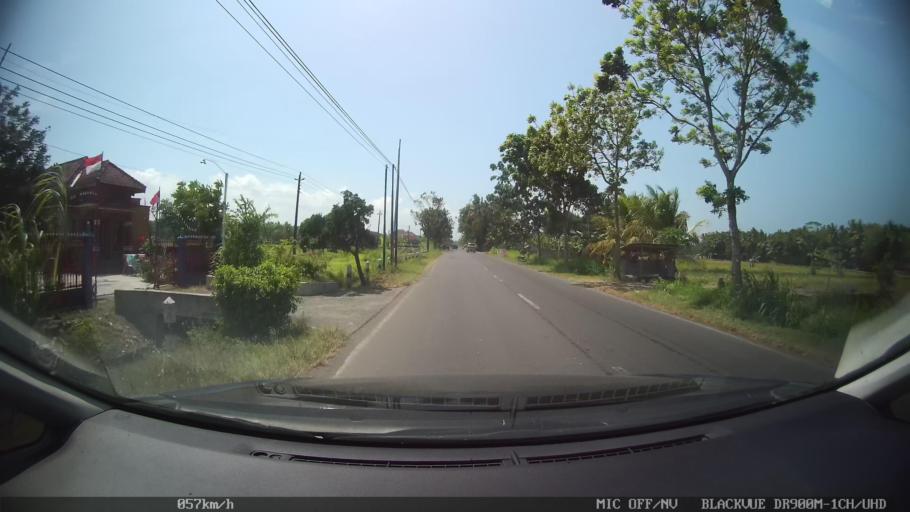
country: ID
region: Daerah Istimewa Yogyakarta
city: Srandakan
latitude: -7.9520
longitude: 110.2031
